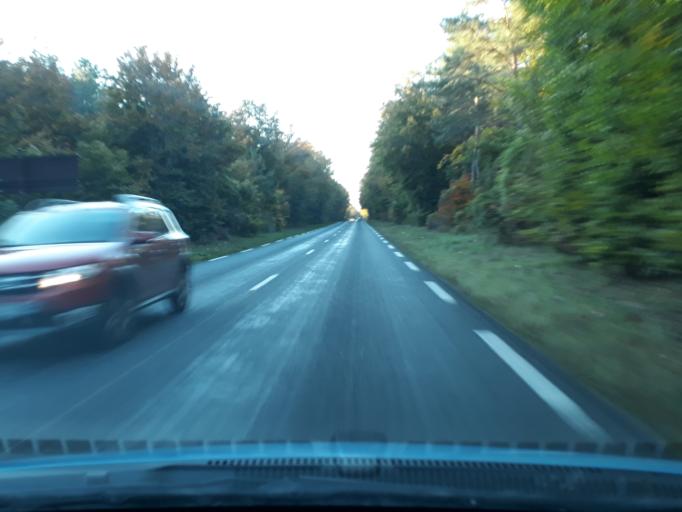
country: FR
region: Ile-de-France
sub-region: Departement de Seine-et-Marne
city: Bois-le-Roi
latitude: 48.4460
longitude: 2.7158
